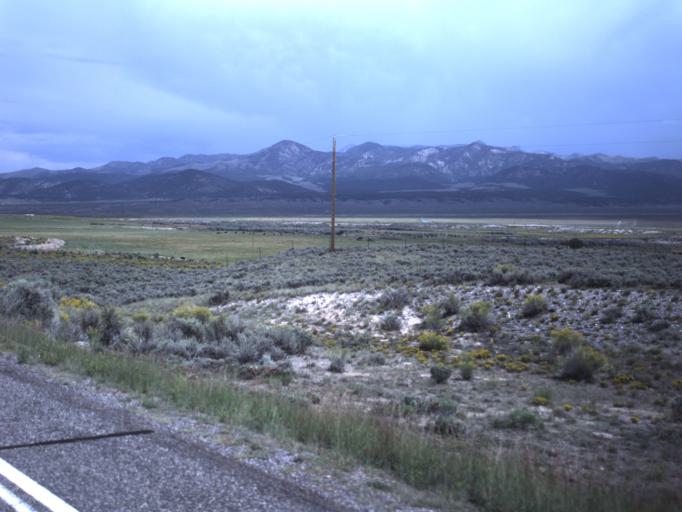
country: US
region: Utah
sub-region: Garfield County
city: Panguitch
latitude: 37.9706
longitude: -112.4092
